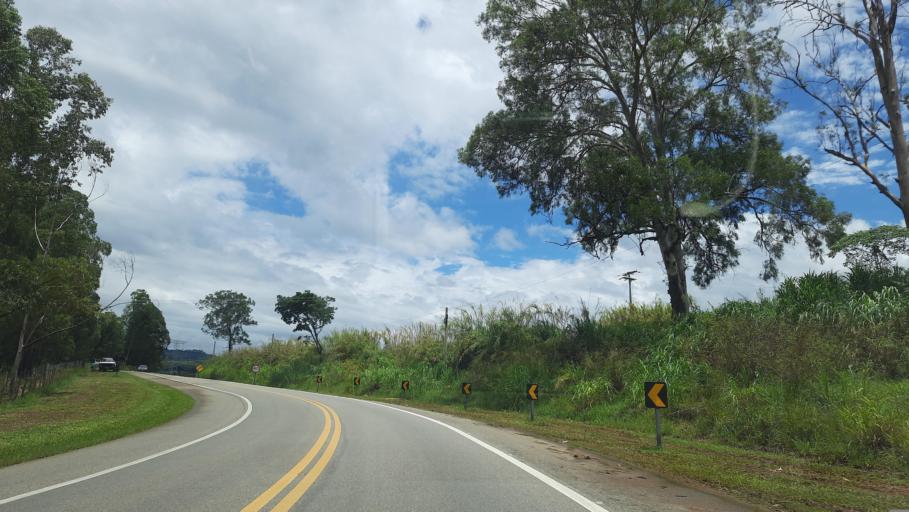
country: BR
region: Sao Paulo
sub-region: Vargem Grande Do Sul
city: Vargem Grande do Sul
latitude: -21.8002
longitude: -46.8108
